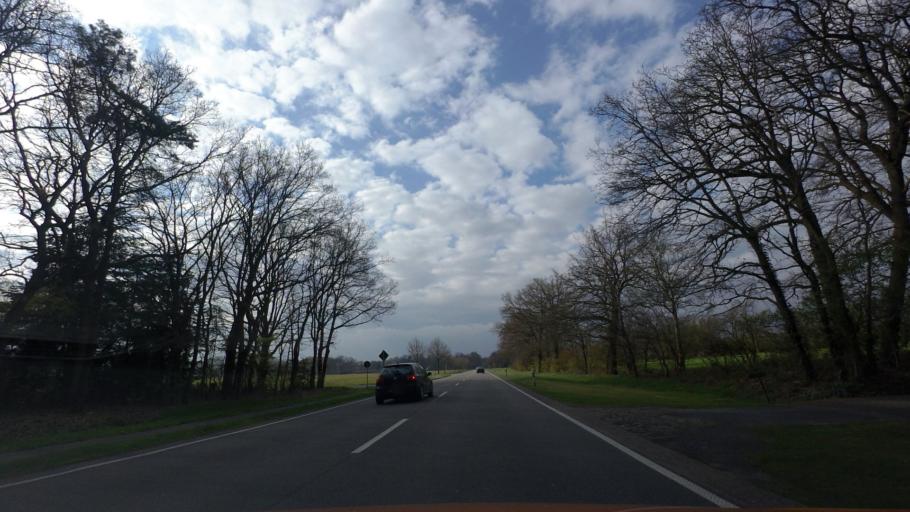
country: DE
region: Lower Saxony
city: Bosel
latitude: 52.9759
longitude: 7.9069
